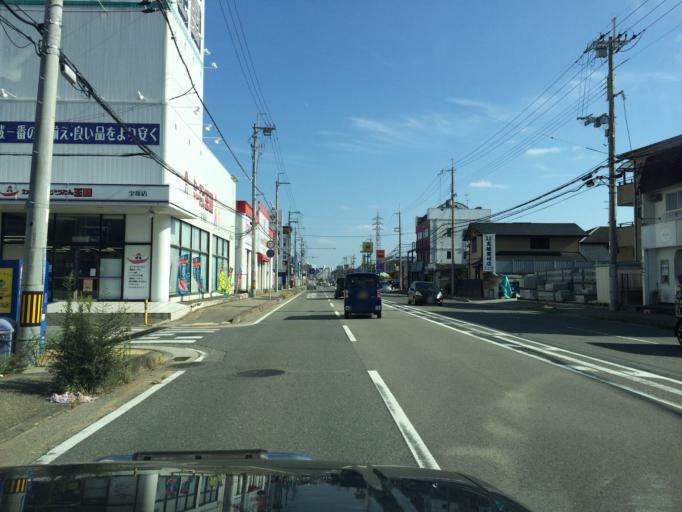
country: JP
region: Hyogo
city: Takarazuka
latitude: 34.7951
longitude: 135.3746
